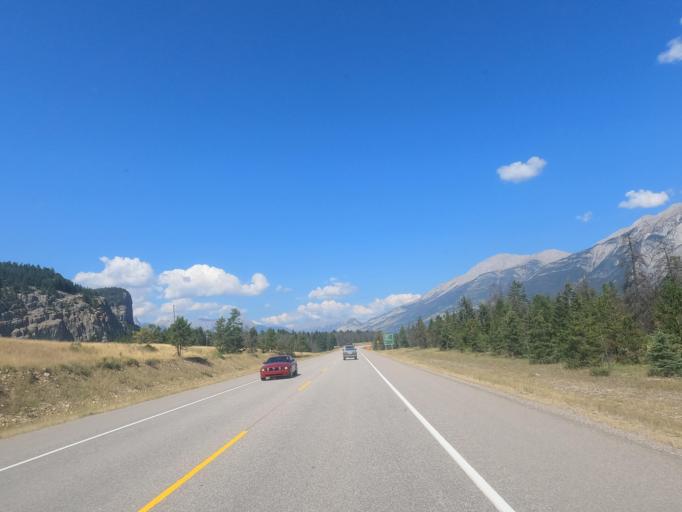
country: CA
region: Alberta
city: Jasper Park Lodge
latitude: 52.9352
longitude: -118.0384
